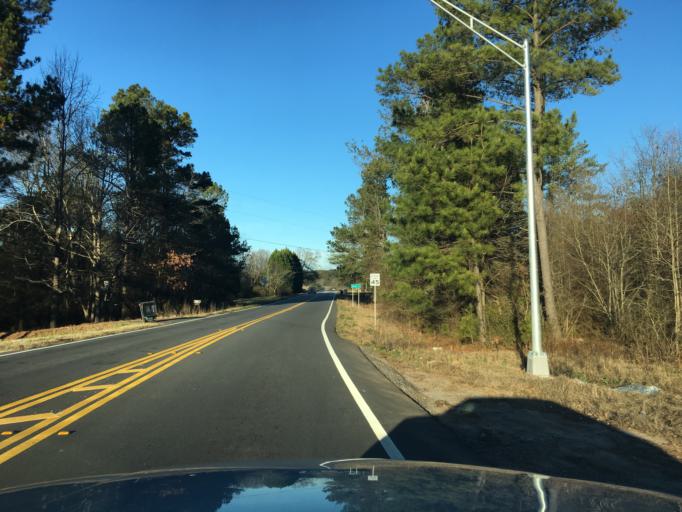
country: US
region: Georgia
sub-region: Barrow County
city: Auburn
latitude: 33.9017
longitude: -83.8007
